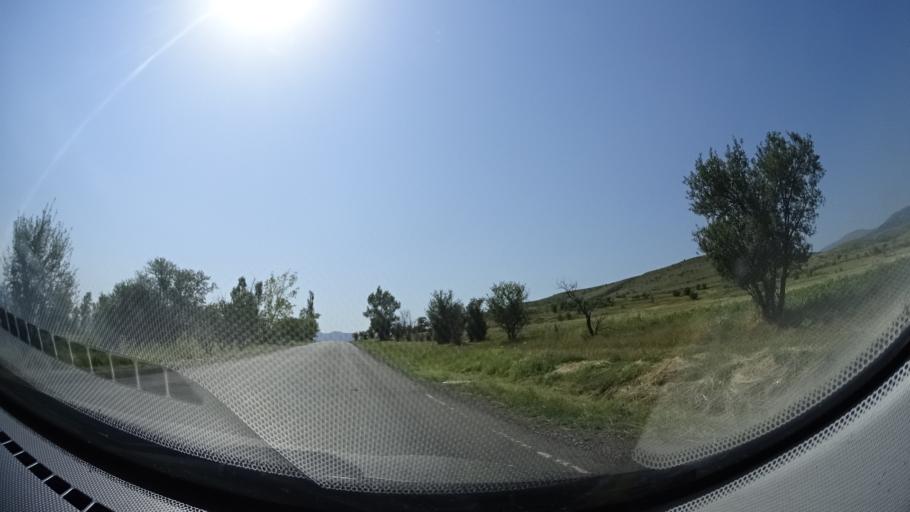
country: GE
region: Samtskhe-Javakheti
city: Akhaltsikhe
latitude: 41.6411
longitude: 43.0280
